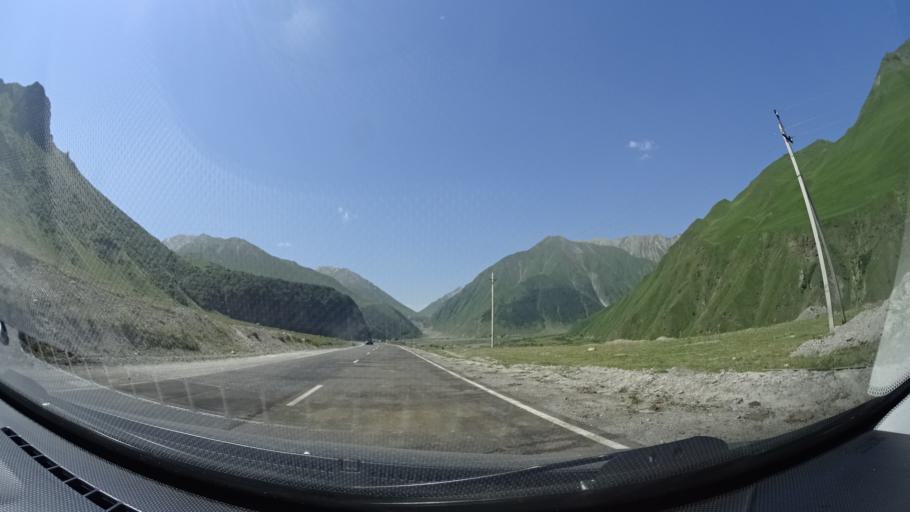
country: GE
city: Gudauri
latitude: 42.5728
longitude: 44.5236
